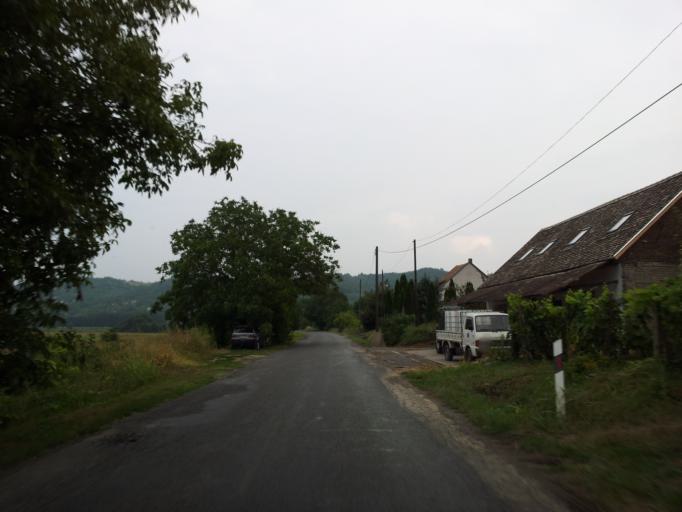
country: HU
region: Tolna
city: Szentgalpuszta
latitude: 46.3826
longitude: 18.6673
